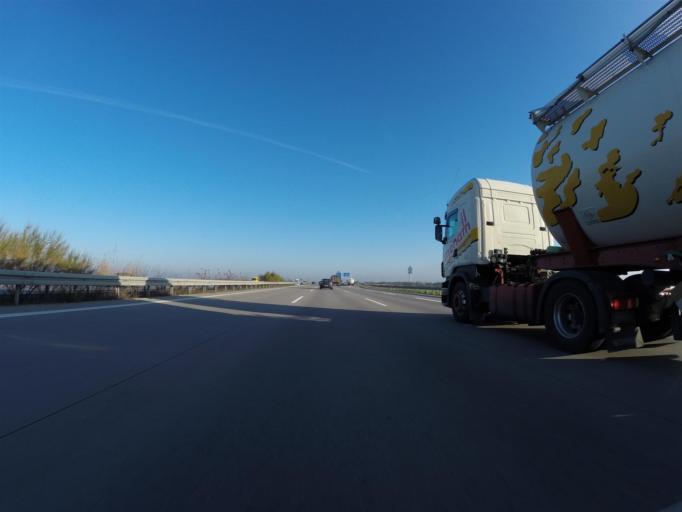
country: DE
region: Saxony-Anhalt
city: Nessa
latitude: 51.1728
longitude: 12.0004
